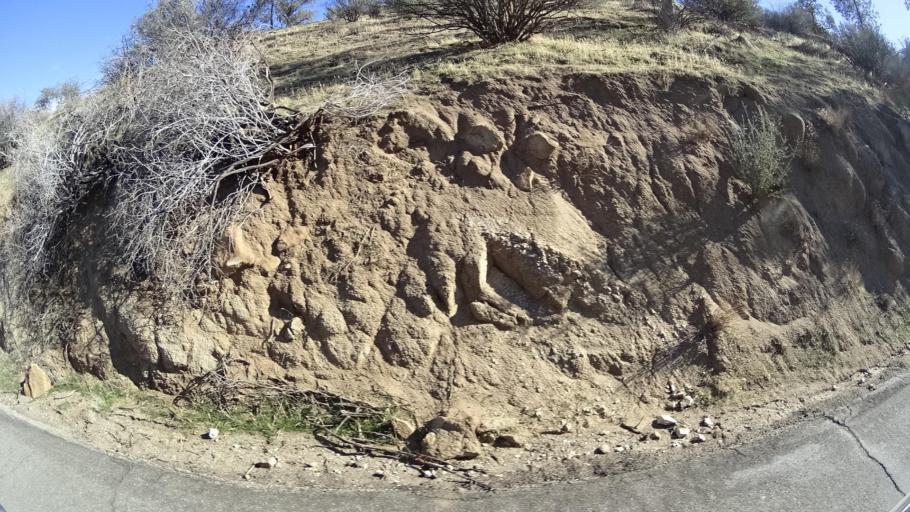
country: US
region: California
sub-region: Kern County
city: Bodfish
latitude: 35.5764
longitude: -118.5423
